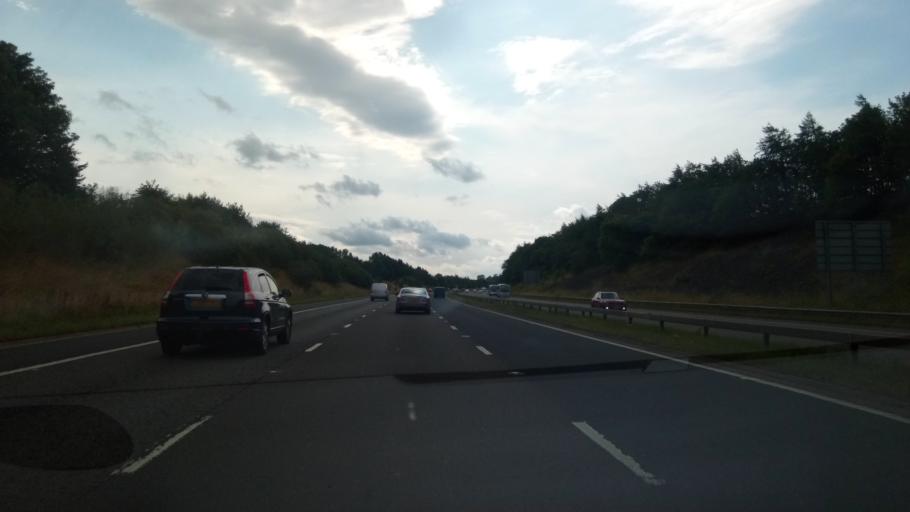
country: GB
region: England
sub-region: Cumbria
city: Penrith
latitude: 54.6463
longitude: -2.7436
